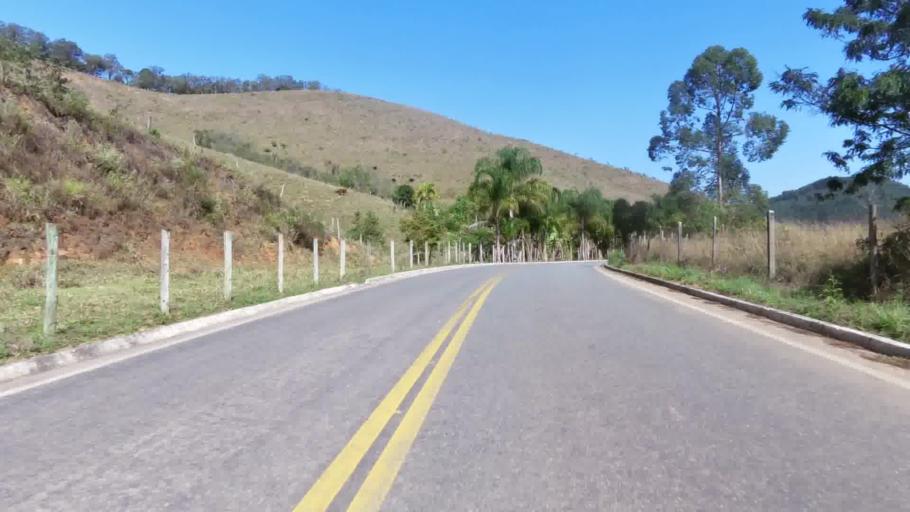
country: BR
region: Espirito Santo
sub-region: Alfredo Chaves
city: Alfredo Chaves
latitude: -20.5658
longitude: -40.8142
